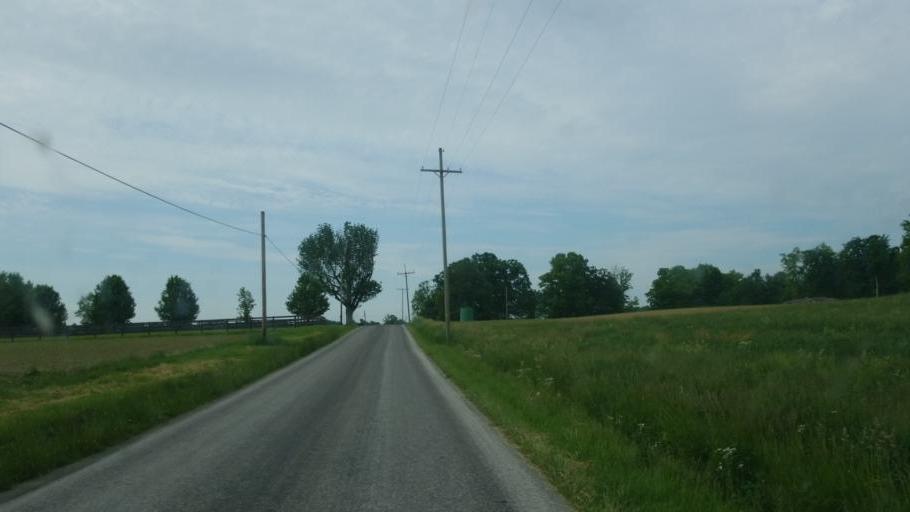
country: US
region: Ohio
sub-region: Wayne County
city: Apple Creek
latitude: 40.7379
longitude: -81.7552
